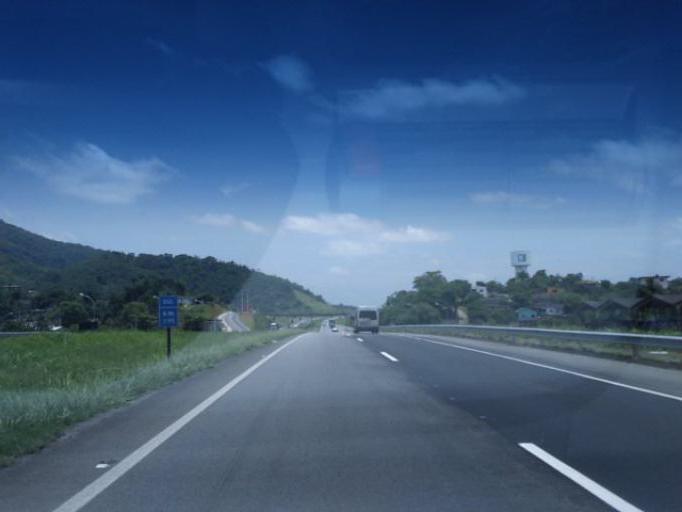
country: BR
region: Sao Paulo
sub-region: Miracatu
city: Miracatu
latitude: -24.2887
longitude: -47.4607
